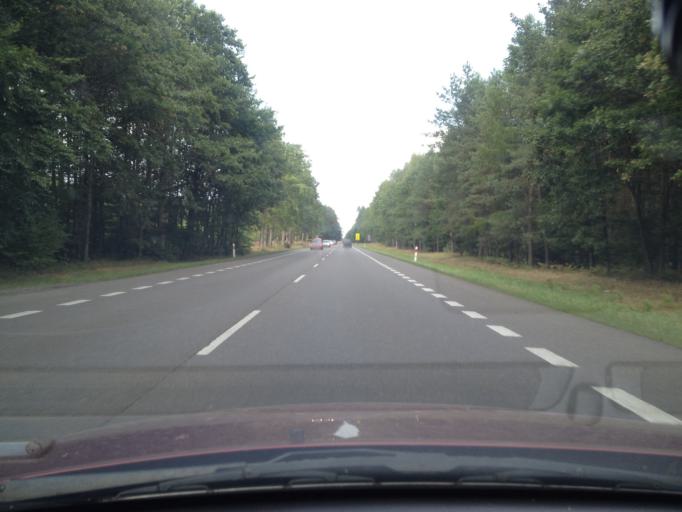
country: PL
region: West Pomeranian Voivodeship
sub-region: Powiat goleniowski
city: Przybiernow
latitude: 53.6906
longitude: 14.7951
